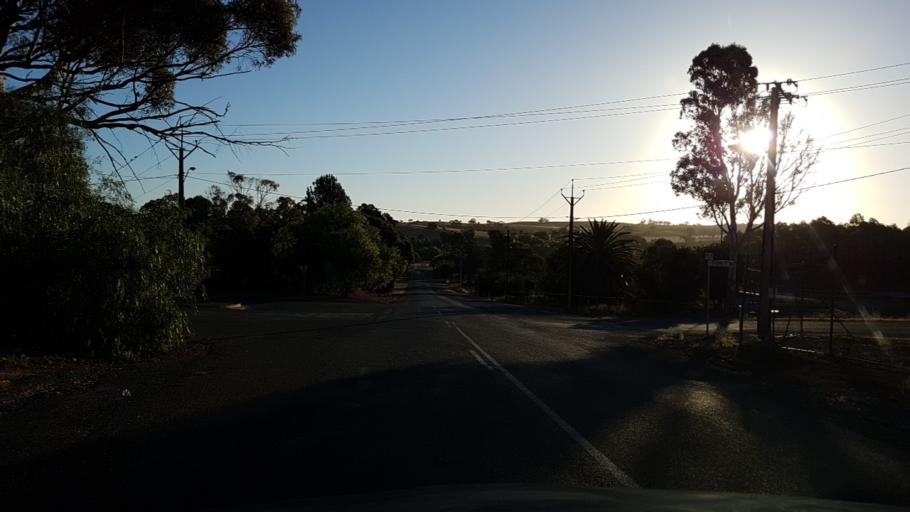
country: AU
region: South Australia
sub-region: Clare and Gilbert Valleys
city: Clare
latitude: -34.0224
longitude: 138.6914
